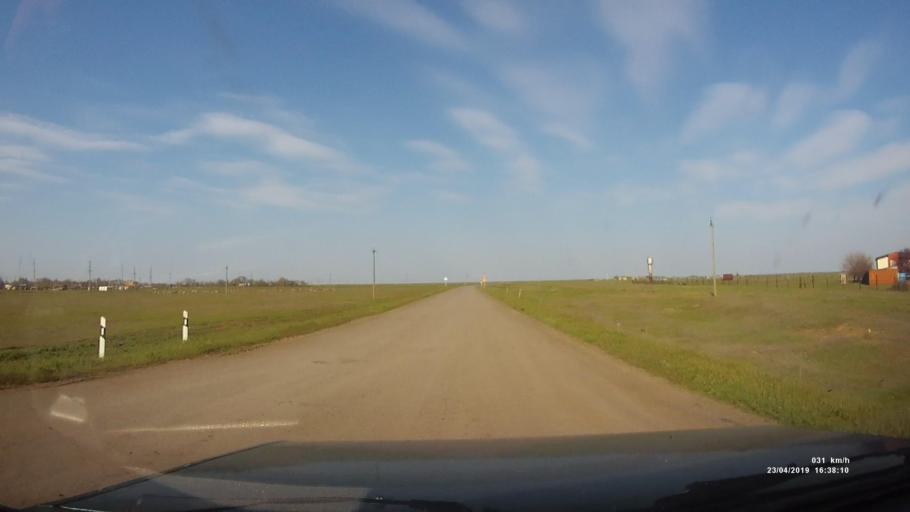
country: RU
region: Kalmykiya
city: Priyutnoye
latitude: 46.3345
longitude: 43.1510
